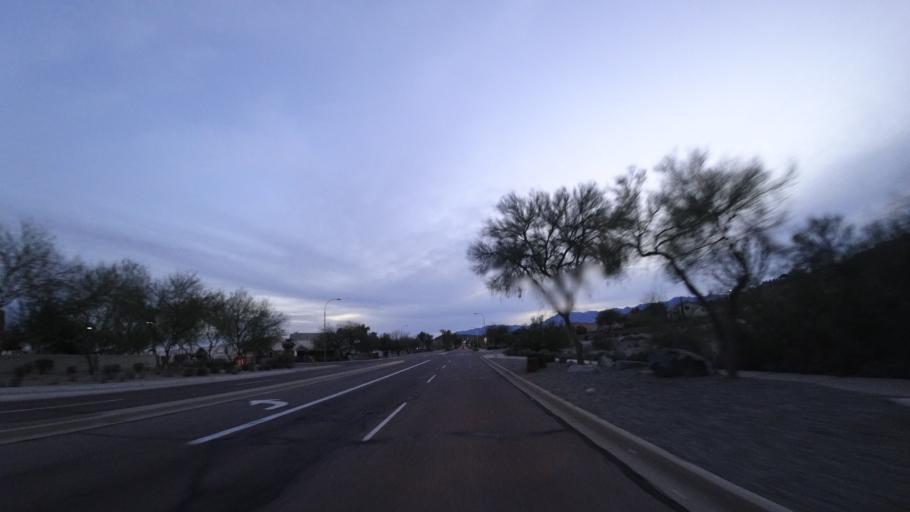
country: US
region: Arizona
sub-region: Maricopa County
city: Guadalupe
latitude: 33.3030
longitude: -112.0577
